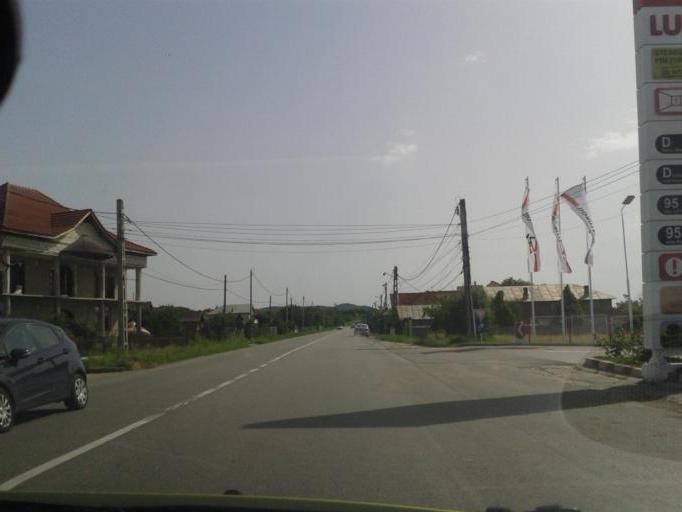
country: RO
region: Valcea
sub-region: Municipiul Ramnicu Valcea
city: Stolniceni
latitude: 45.0555
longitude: 24.2874
